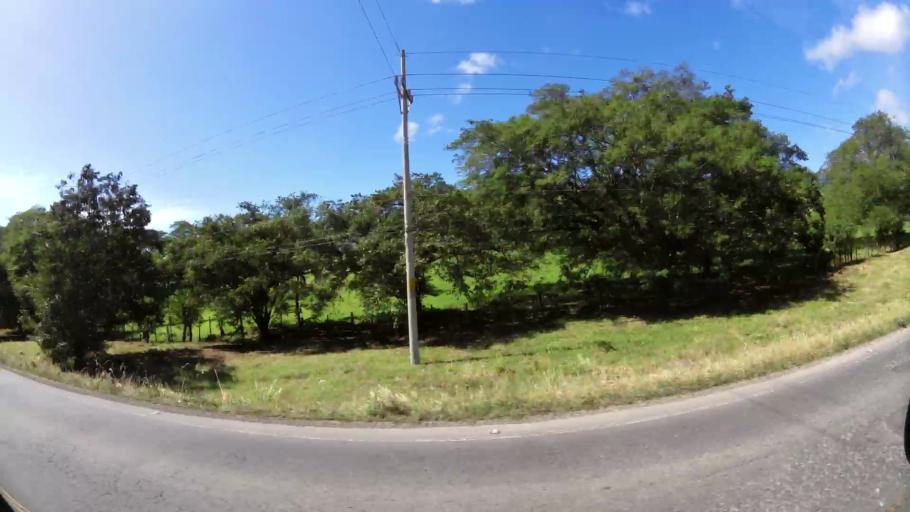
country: CR
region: Guanacaste
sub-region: Canton de Canas
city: Canas
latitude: 10.4009
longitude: -85.0815
